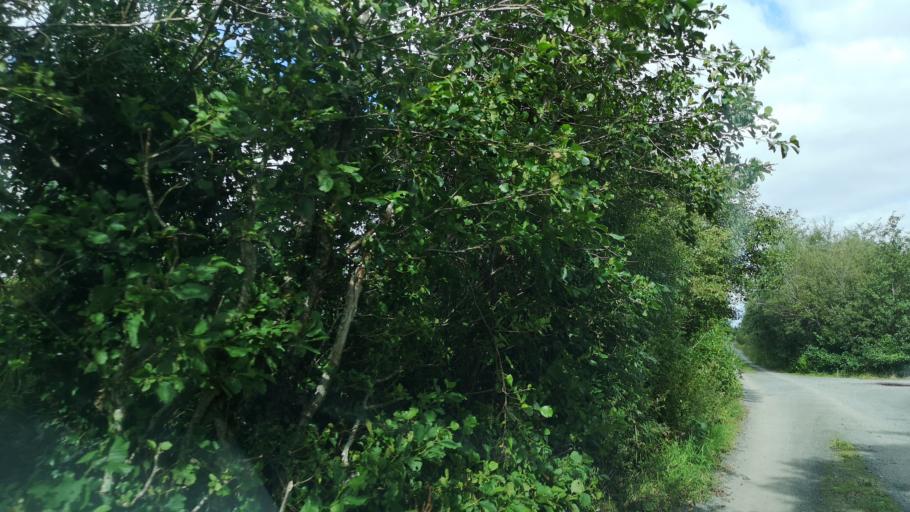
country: IE
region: Connaught
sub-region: County Galway
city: Moycullen
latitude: 53.3200
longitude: -9.1325
